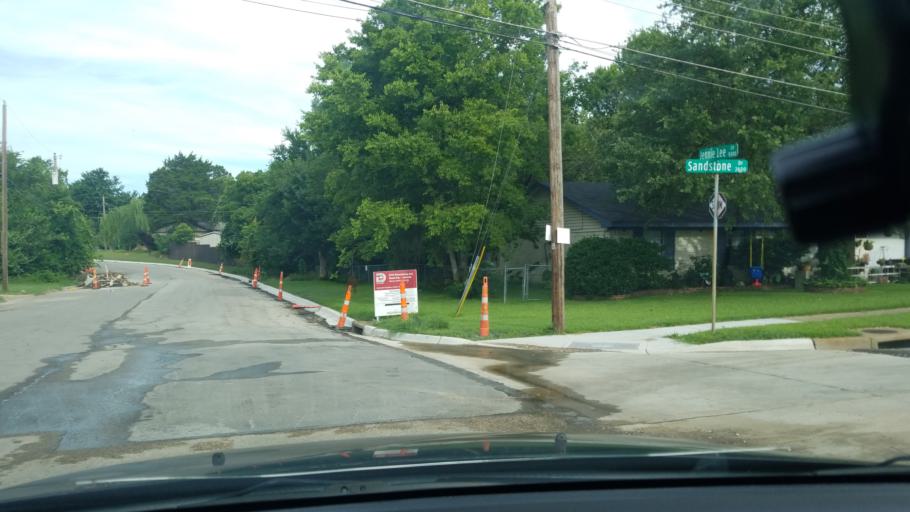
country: US
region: Texas
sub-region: Dallas County
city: Balch Springs
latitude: 32.7564
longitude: -96.6629
